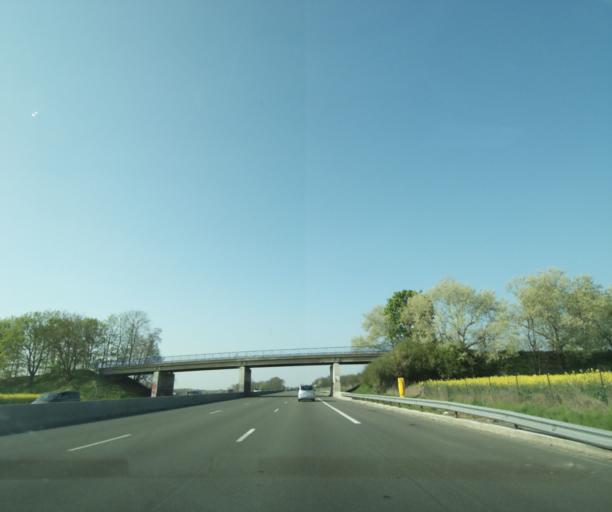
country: FR
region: Ile-de-France
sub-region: Departement de l'Essonne
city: Le Coudray-Montceaux
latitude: 48.5424
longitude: 2.4978
